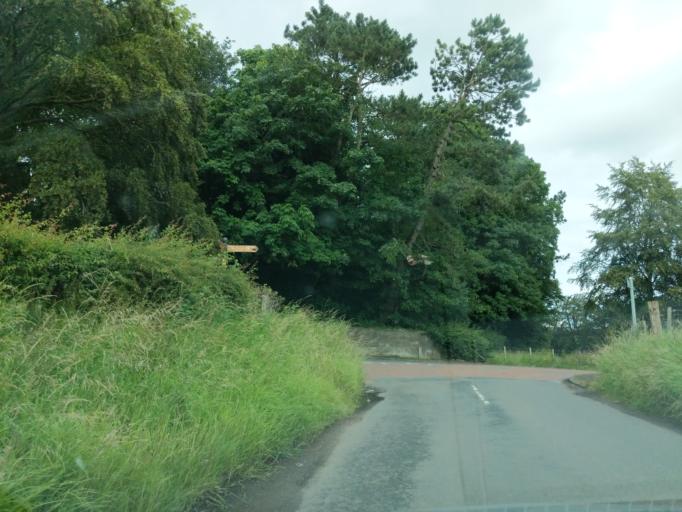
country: GB
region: Scotland
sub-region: South Lanarkshire
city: Dalserf
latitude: 55.7216
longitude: -3.9209
